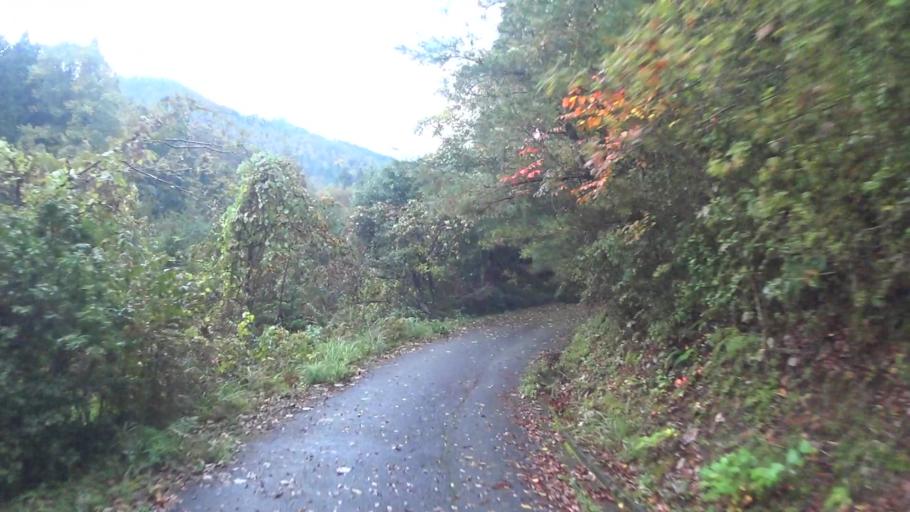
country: JP
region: Kyoto
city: Ayabe
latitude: 35.2646
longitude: 135.2255
